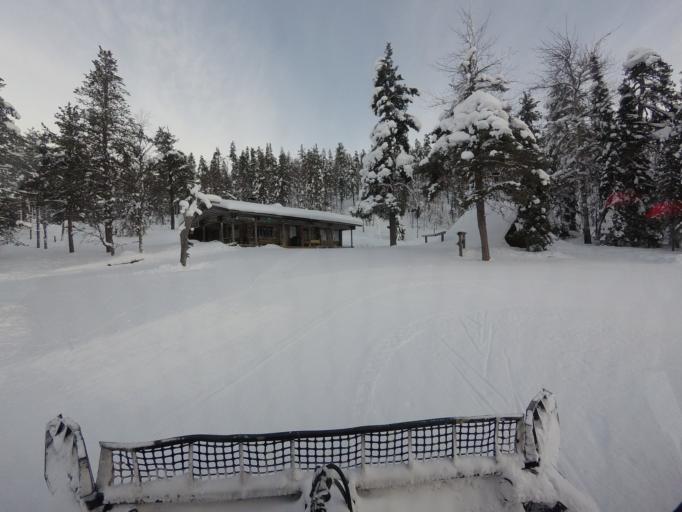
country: FI
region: Lapland
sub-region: Tunturi-Lappi
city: Kolari
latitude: 67.6584
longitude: 24.2536
